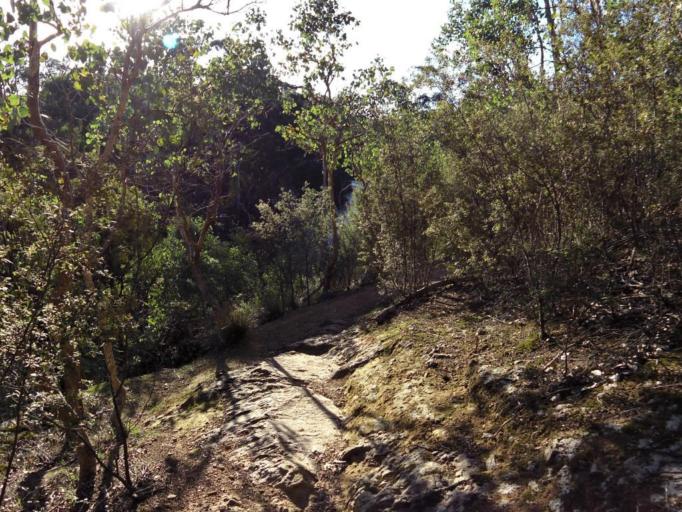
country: AU
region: Victoria
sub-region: Manningham
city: Warrandyte
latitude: -37.7351
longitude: 145.2437
